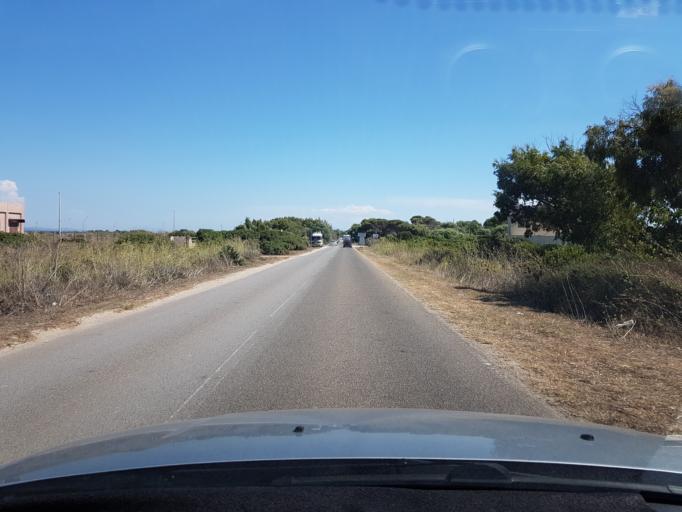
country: IT
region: Sardinia
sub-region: Provincia di Oristano
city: Cabras
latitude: 39.8878
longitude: 8.4361
